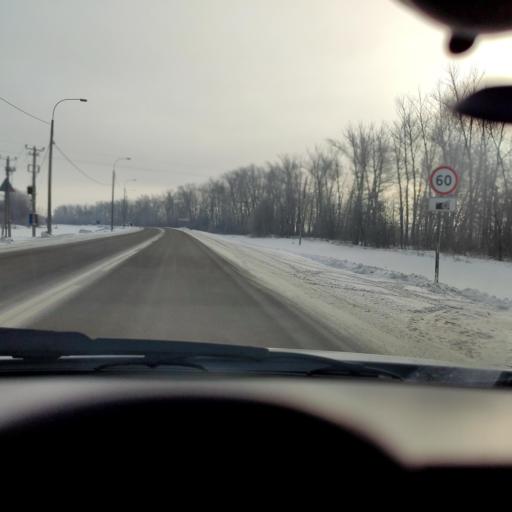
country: RU
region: Kursk
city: Kirovskiy
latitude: 51.6776
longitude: 36.5895
